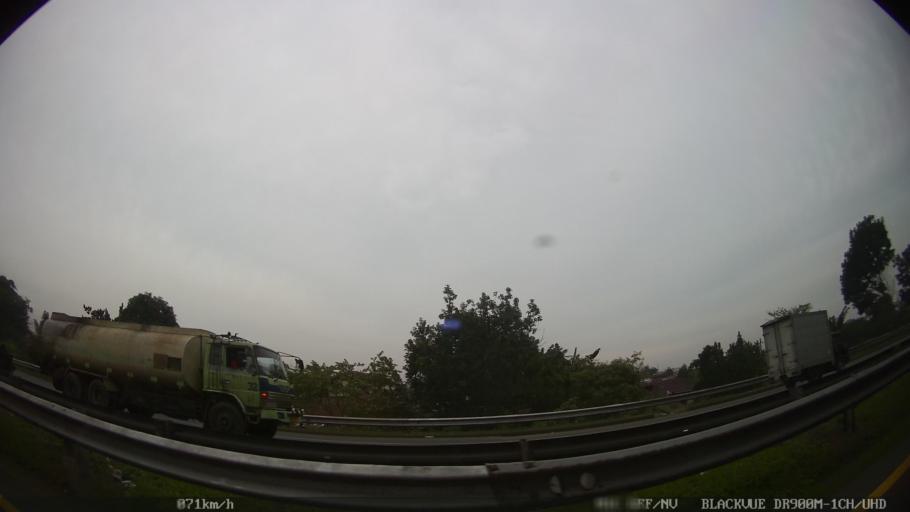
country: ID
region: North Sumatra
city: Medan
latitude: 3.5801
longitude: 98.7246
